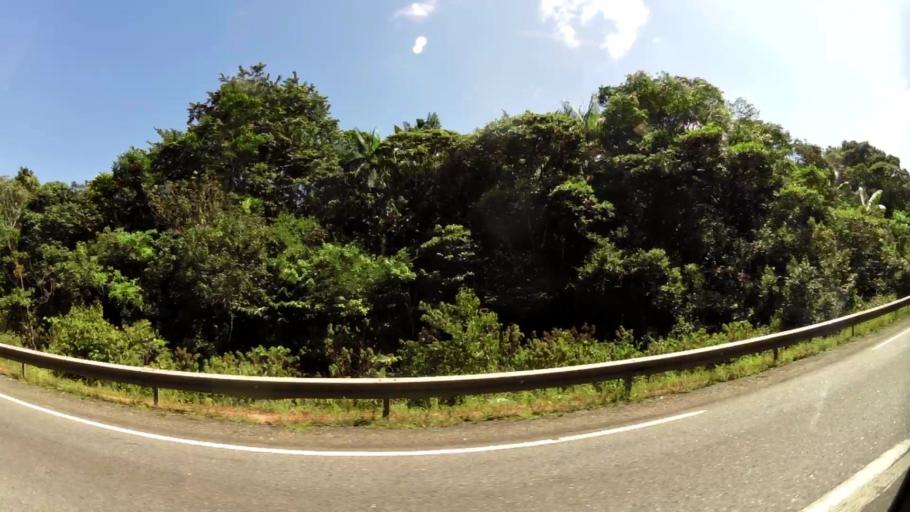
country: GF
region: Guyane
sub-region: Guyane
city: Matoury
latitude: 4.8370
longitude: -52.3415
